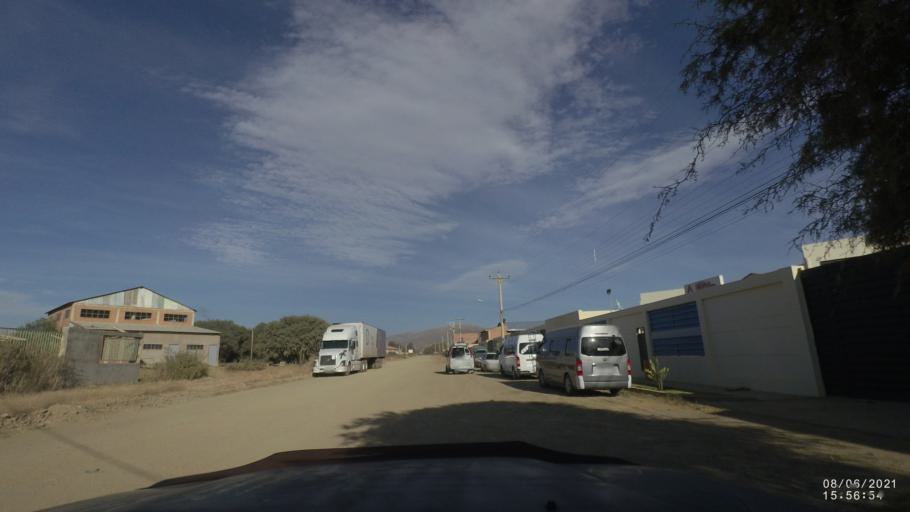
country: BO
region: Cochabamba
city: Capinota
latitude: -17.5594
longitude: -66.2522
